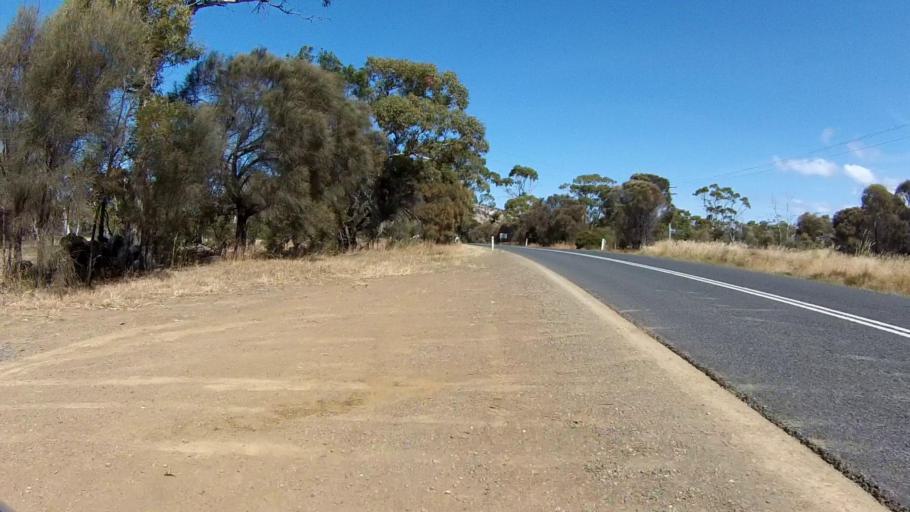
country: AU
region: Tasmania
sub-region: Sorell
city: Sorell
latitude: -42.1452
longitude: 148.0680
